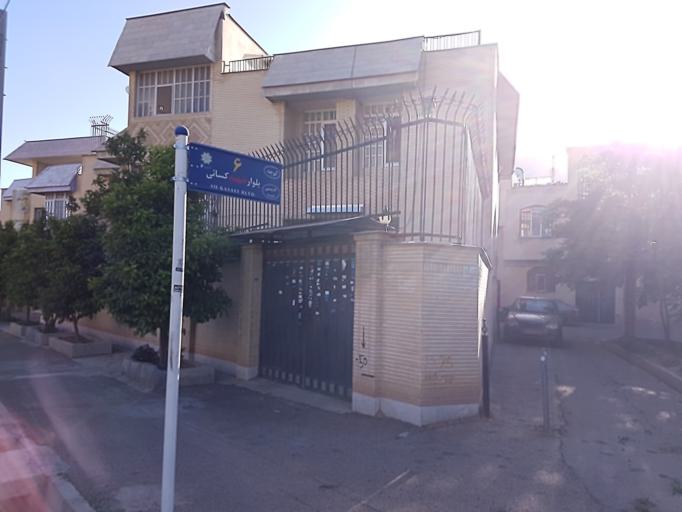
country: IR
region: Fars
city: Shiraz
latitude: 29.6636
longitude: 52.4572
